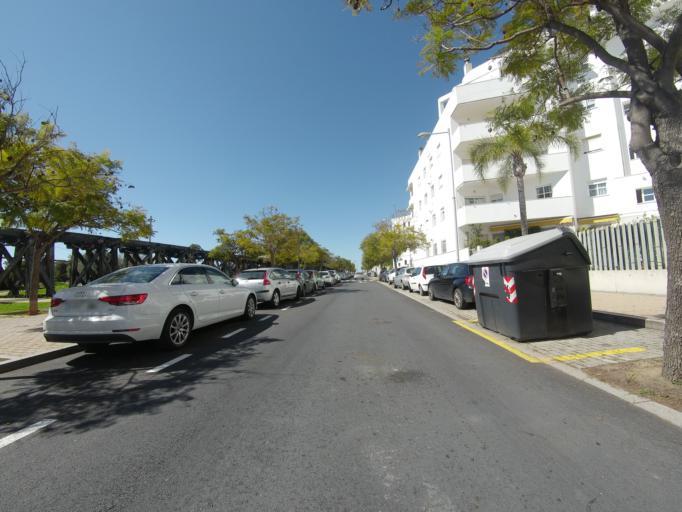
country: ES
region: Andalusia
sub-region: Provincia de Huelva
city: Huelva
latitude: 37.2519
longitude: -6.9547
